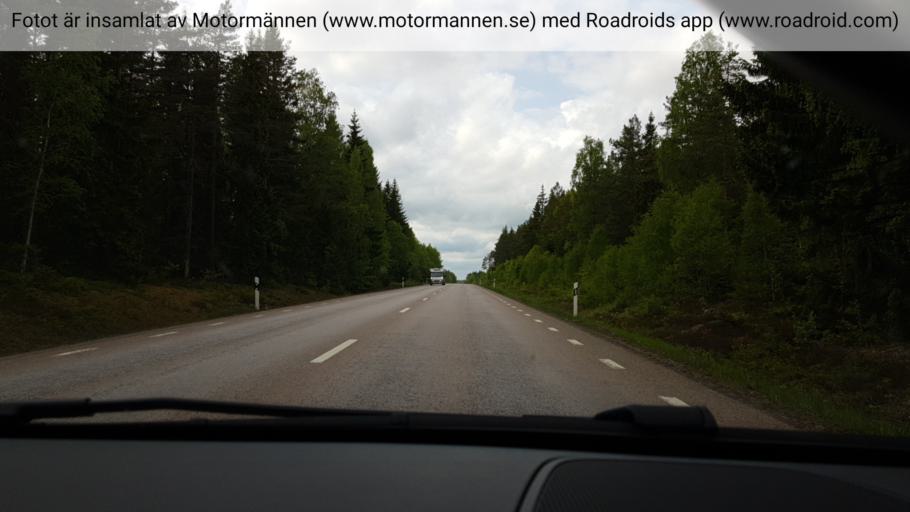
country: SE
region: Uppsala
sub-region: Osthammars Kommun
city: Osterbybruk
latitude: 60.1986
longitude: 17.8092
